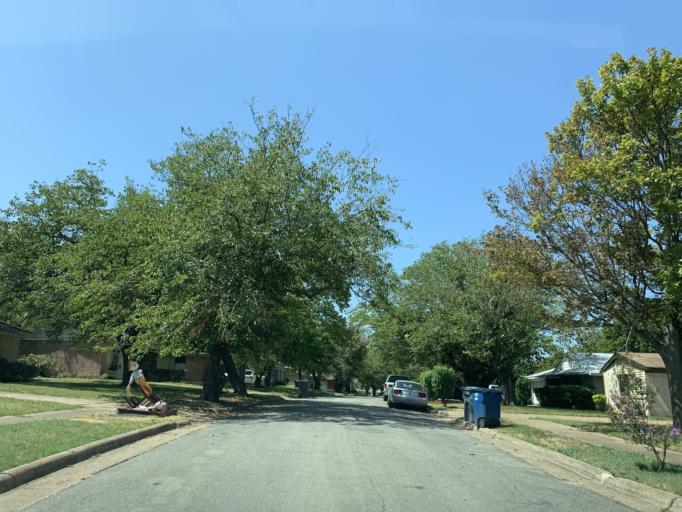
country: US
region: Texas
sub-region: Dallas County
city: Hutchins
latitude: 32.6749
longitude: -96.7499
